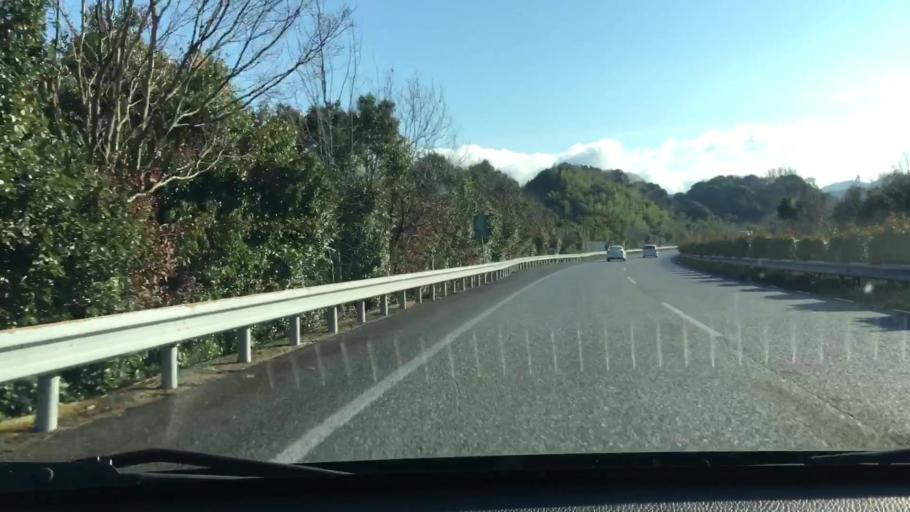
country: JP
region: Kumamoto
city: Hitoyoshi
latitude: 32.1962
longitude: 130.7778
